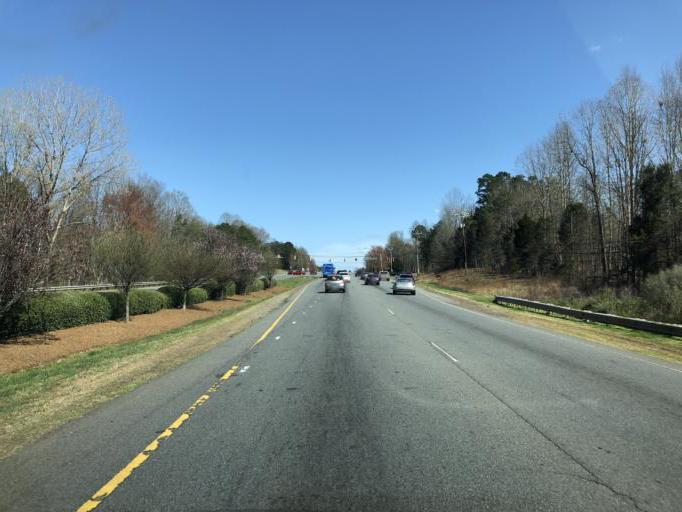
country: US
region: North Carolina
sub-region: Mecklenburg County
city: Huntersville
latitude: 35.3326
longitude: -80.8010
